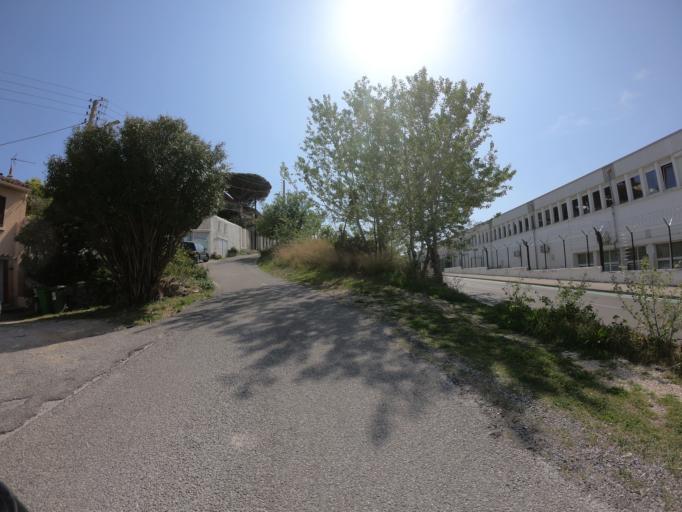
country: FR
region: Provence-Alpes-Cote d'Azur
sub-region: Departement du Var
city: Toulon
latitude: 43.1057
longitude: 5.9297
